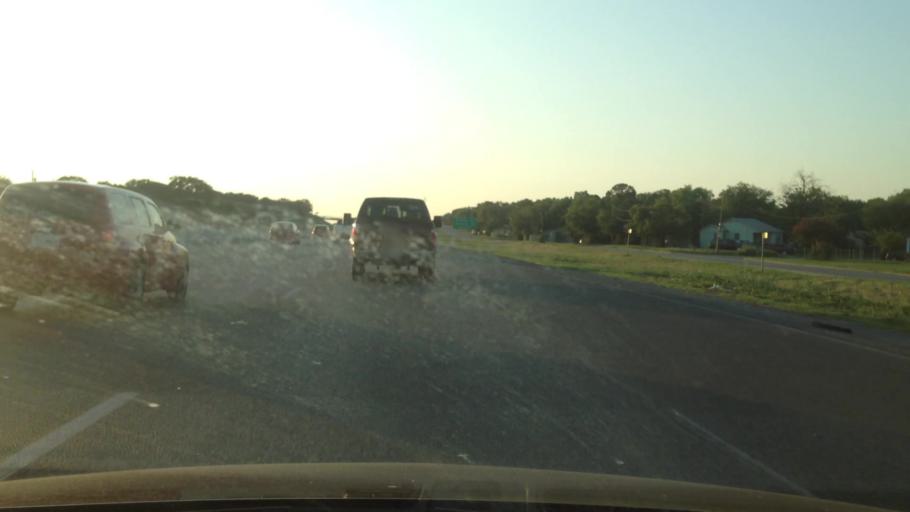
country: US
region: Texas
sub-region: Tarrant County
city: Forest Hill
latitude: 32.7041
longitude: -97.2671
